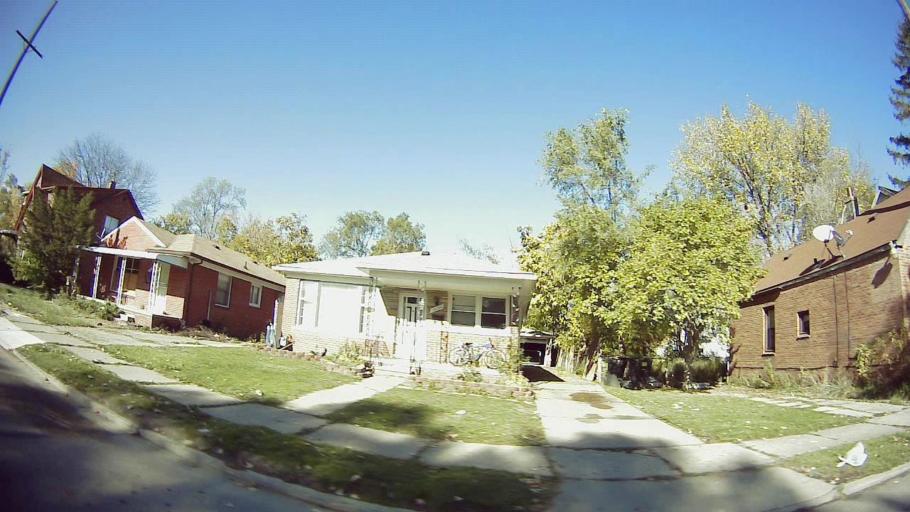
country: US
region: Michigan
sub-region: Wayne County
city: Dearborn Heights
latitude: 42.3505
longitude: -83.2266
